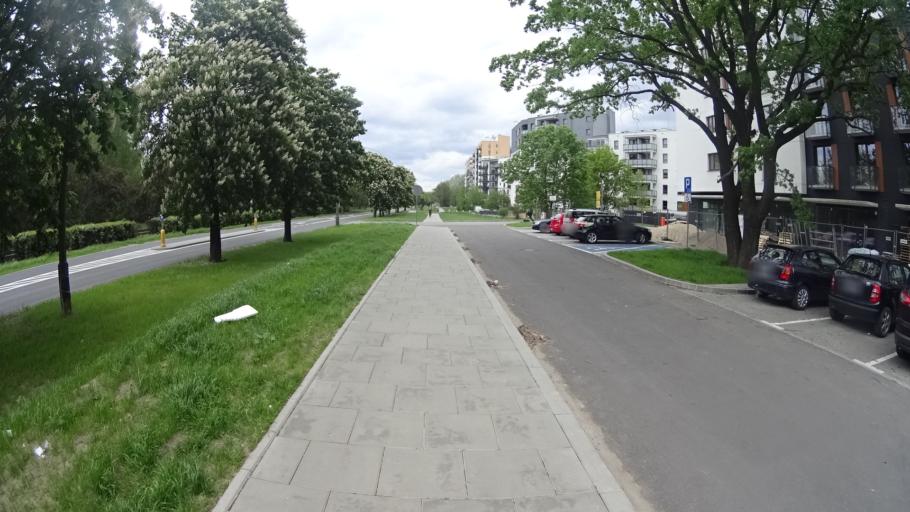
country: PL
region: Masovian Voivodeship
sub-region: Warszawa
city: Bielany
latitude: 52.2854
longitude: 20.9241
